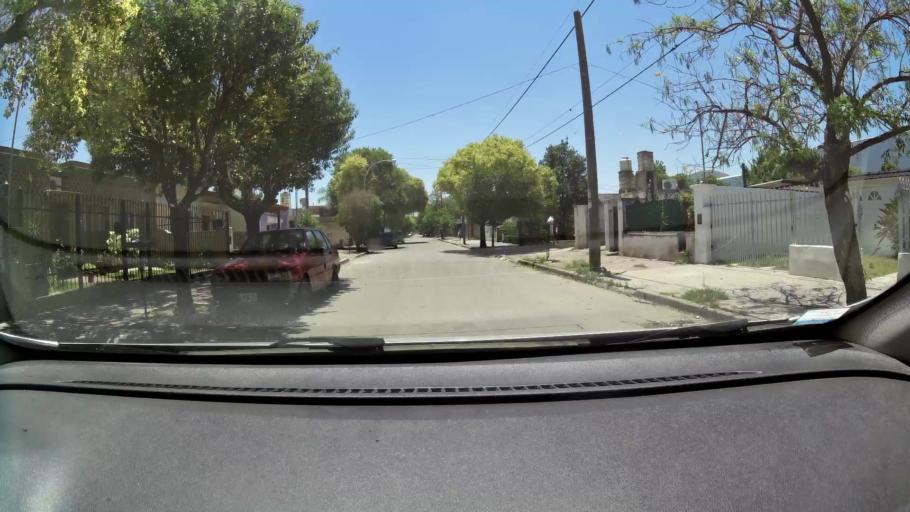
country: AR
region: Cordoba
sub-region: Departamento de Capital
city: Cordoba
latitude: -31.3873
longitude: -64.1304
